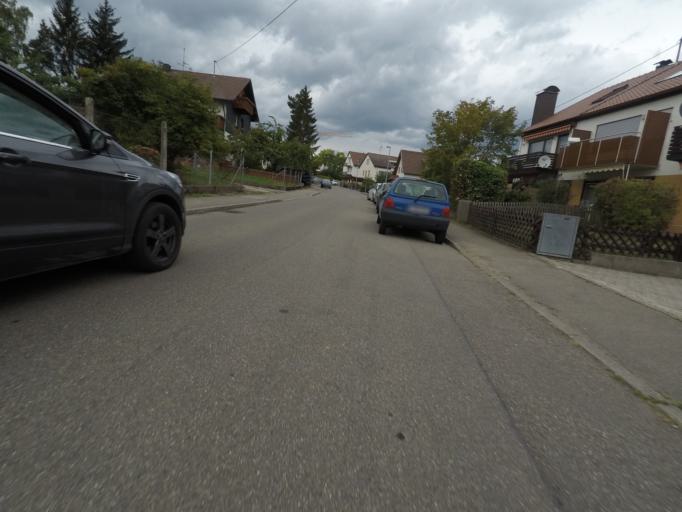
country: DE
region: Baden-Wuerttemberg
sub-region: Regierungsbezirk Stuttgart
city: Filderstadt
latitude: 48.6570
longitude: 9.1988
